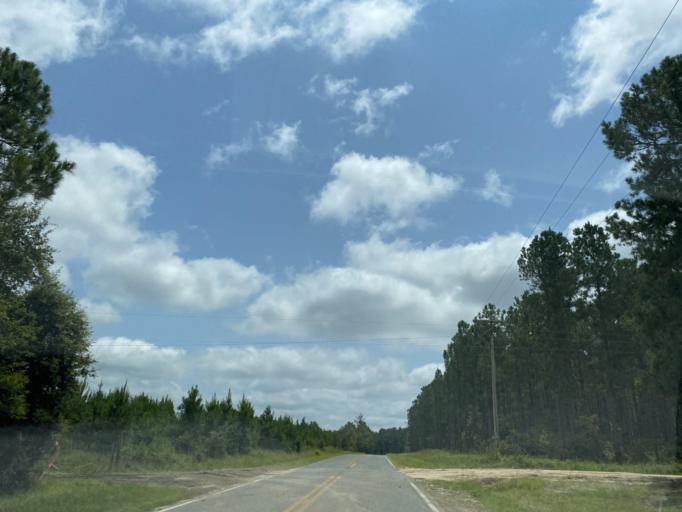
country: US
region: Georgia
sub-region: Wheeler County
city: Alamo
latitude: 32.1164
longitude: -82.7856
